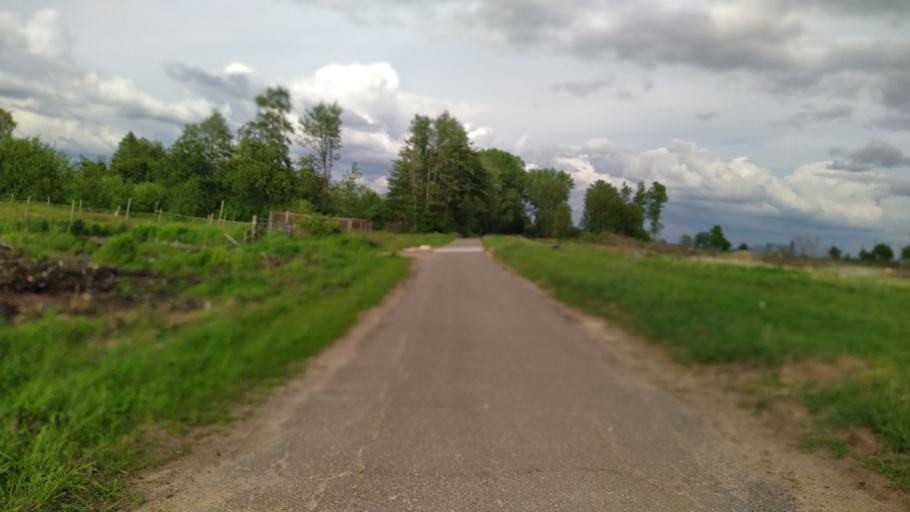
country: DE
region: Lower Saxony
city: Neu Wulmstorf
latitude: 53.4949
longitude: 9.8671
